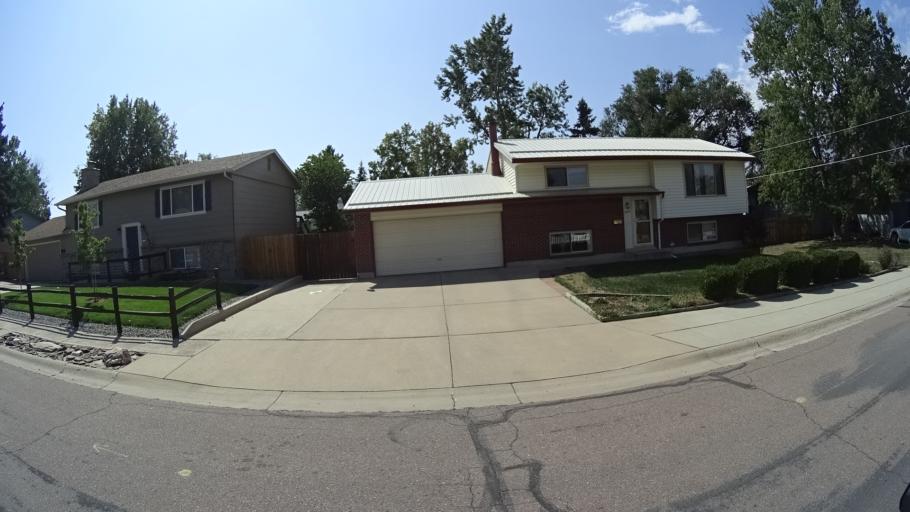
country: US
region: Colorado
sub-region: El Paso County
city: Colorado Springs
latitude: 38.8303
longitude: -104.7660
